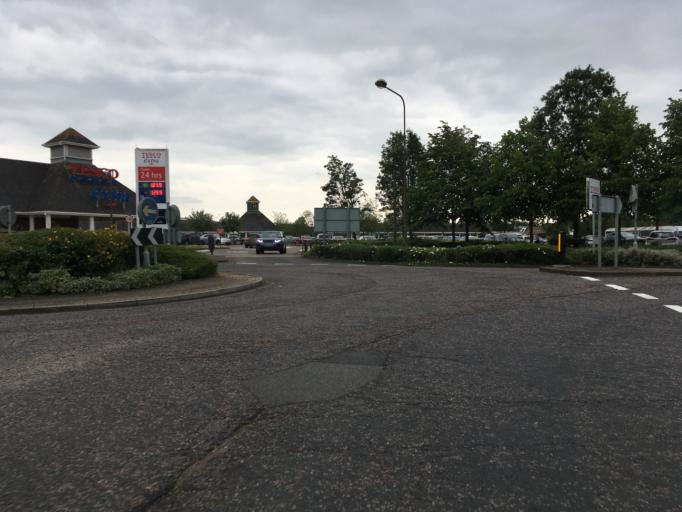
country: GB
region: England
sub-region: Milton Keynes
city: Broughton
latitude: 52.0374
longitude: -0.6887
